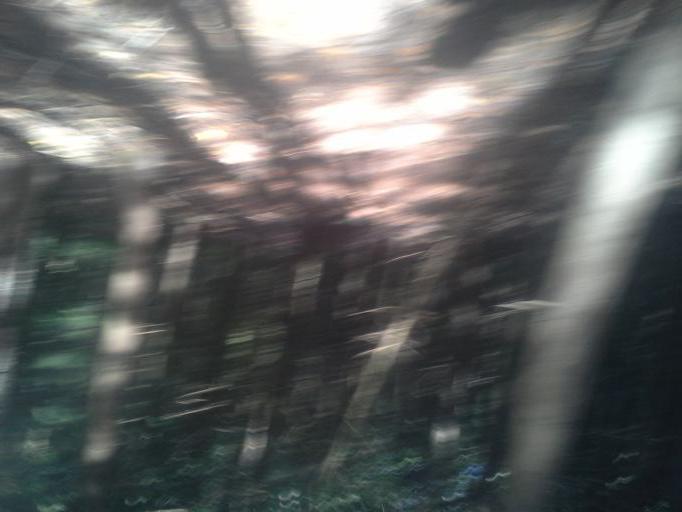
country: RU
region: Moskovskaya
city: Kievskij
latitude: 55.3466
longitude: 36.9584
